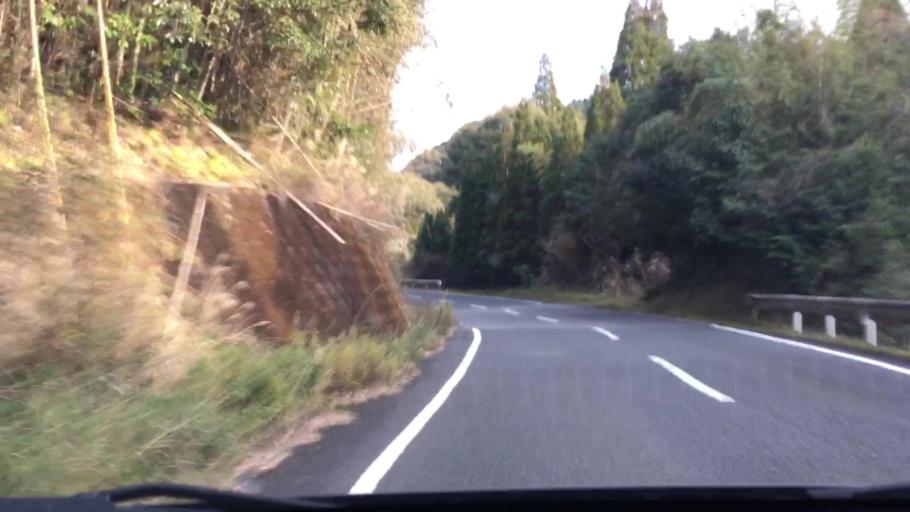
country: JP
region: Miyazaki
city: Nichinan
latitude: 31.5907
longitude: 131.3046
